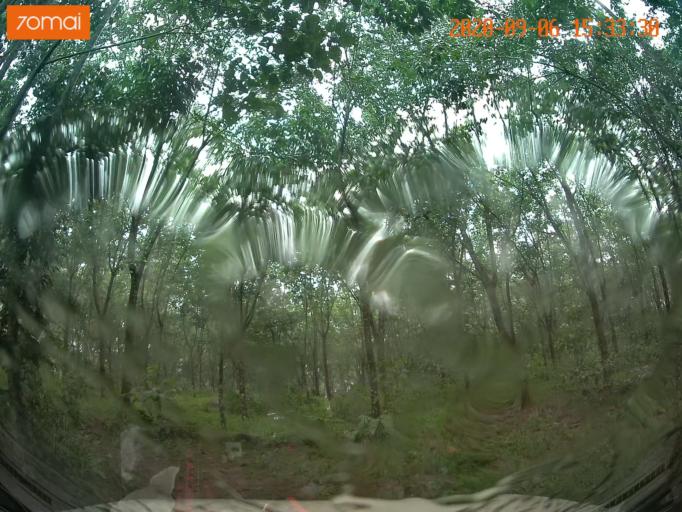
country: IN
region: Kerala
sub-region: Kottayam
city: Palackattumala
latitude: 9.7920
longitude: 76.5625
